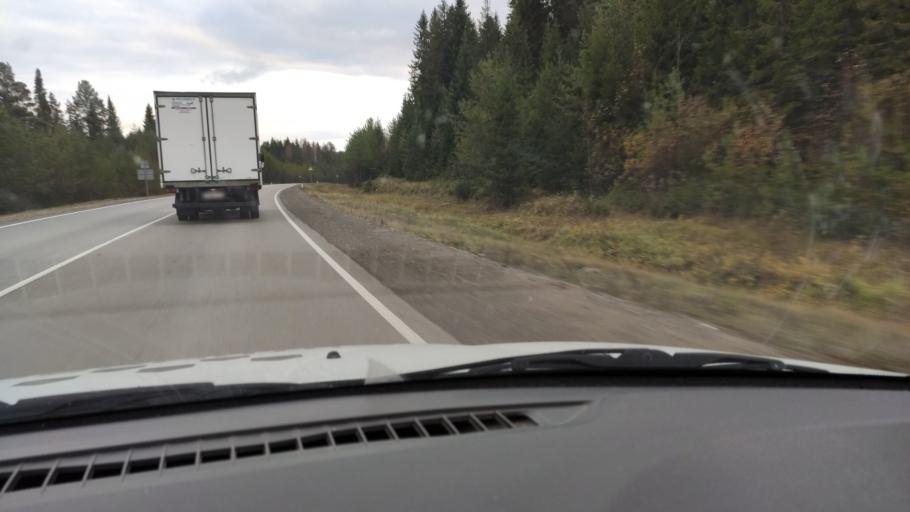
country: RU
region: Kirov
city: Chernaya Kholunitsa
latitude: 58.8517
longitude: 51.7386
